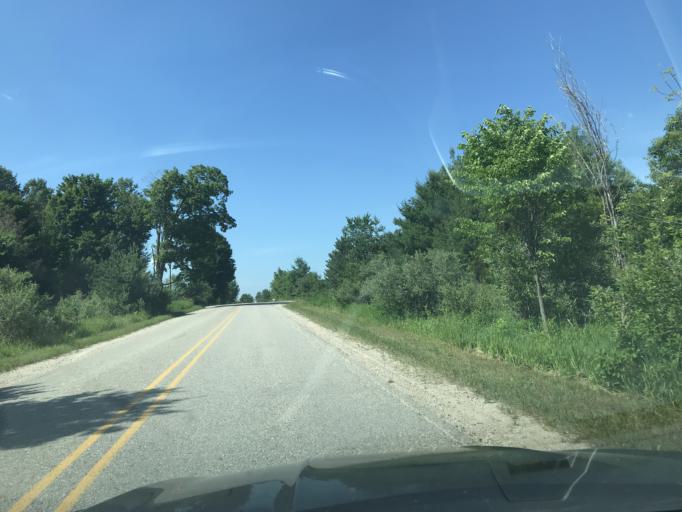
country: US
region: Michigan
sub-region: Cheboygan County
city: Cheboygan
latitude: 45.6209
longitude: -84.6714
